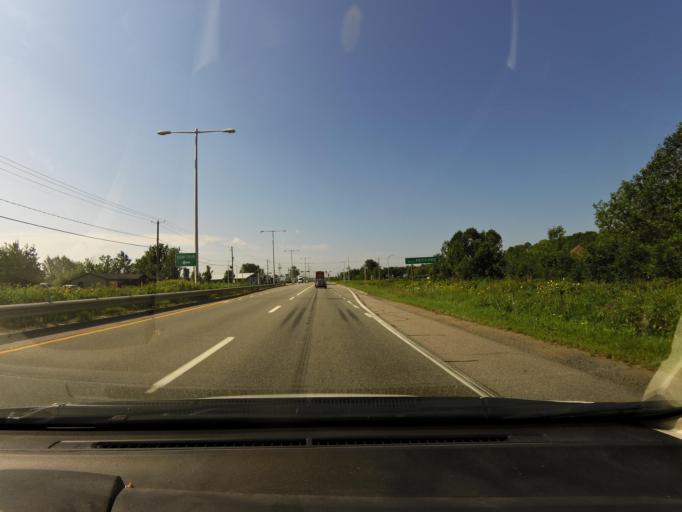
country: CA
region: Quebec
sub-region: Capitale-Nationale
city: Chateau-Richer
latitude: 46.9380
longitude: -71.0560
